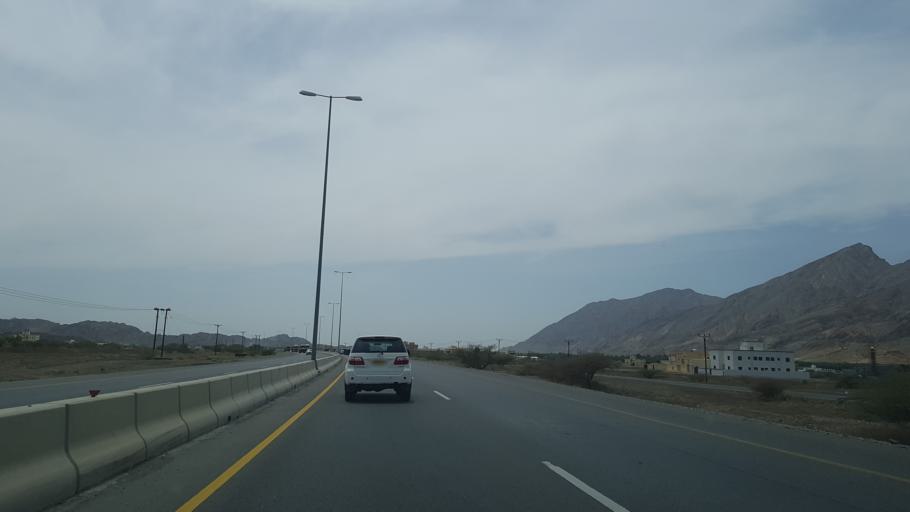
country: OM
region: Muhafazat ad Dakhiliyah
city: Izki
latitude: 23.0153
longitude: 57.7926
